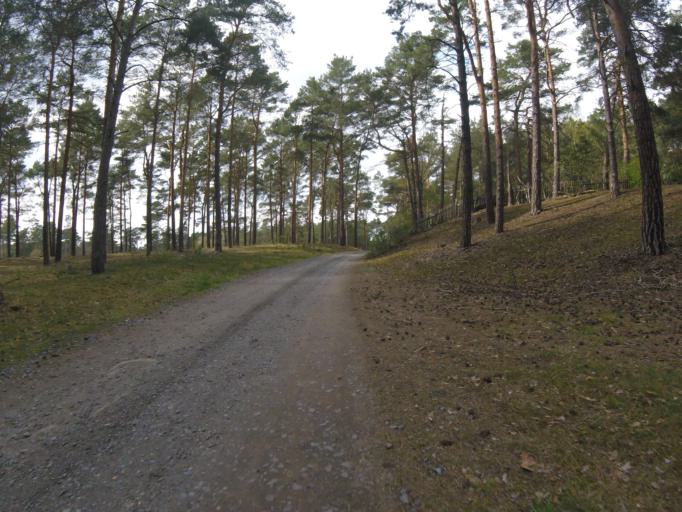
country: DE
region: Brandenburg
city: Gross Koris
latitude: 52.1730
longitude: 13.6601
